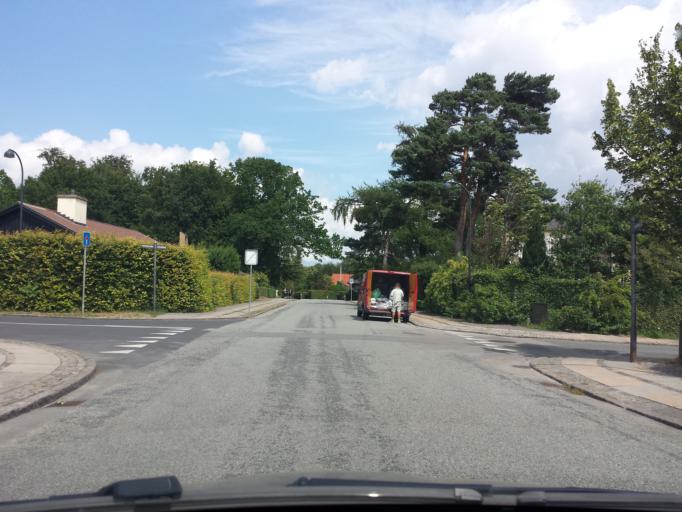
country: DK
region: Capital Region
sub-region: Gentofte Kommune
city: Charlottenlund
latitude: 55.7635
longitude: 12.5702
